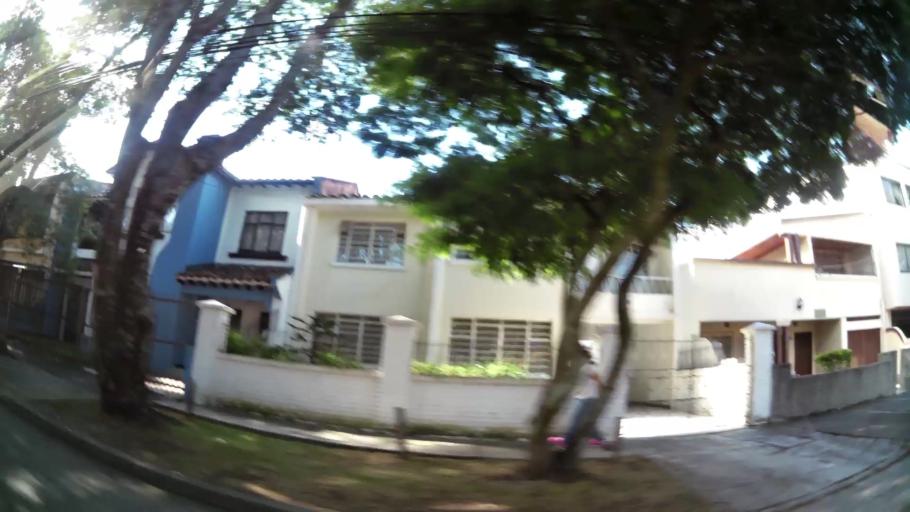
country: CO
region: Valle del Cauca
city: Cali
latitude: 3.4325
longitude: -76.5381
